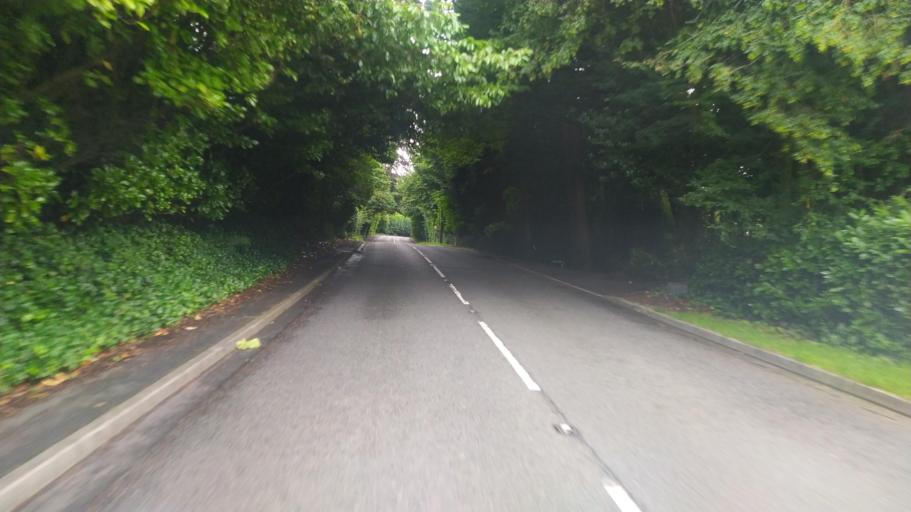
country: GB
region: England
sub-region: Hampshire
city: Liss
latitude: 51.0347
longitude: -0.8780
